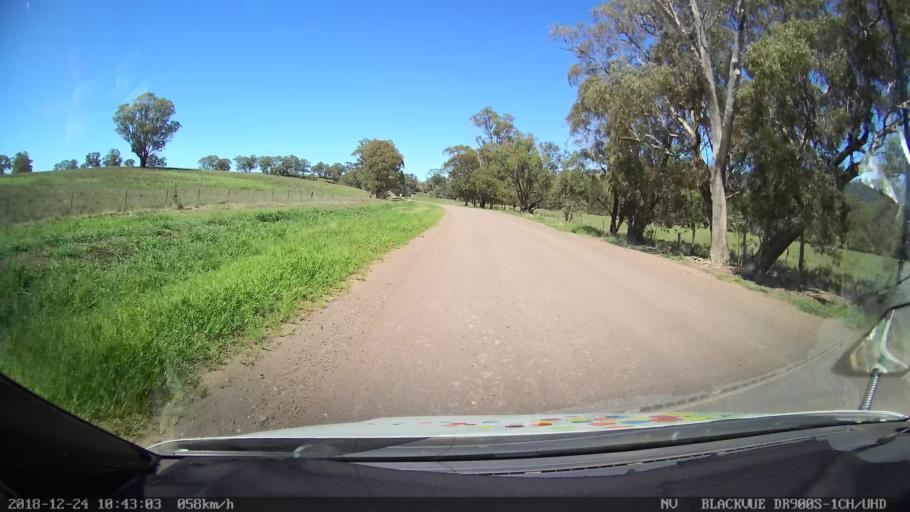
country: AU
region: New South Wales
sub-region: Upper Hunter Shire
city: Merriwa
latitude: -31.8801
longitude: 150.4488
